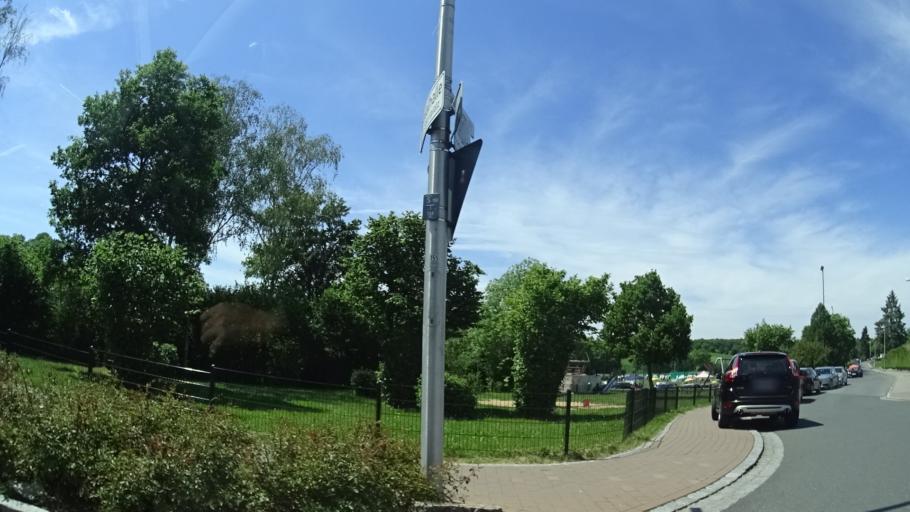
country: DE
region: Bavaria
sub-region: Regierungsbezirk Unterfranken
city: Poppenhausen
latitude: 50.1022
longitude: 10.1429
